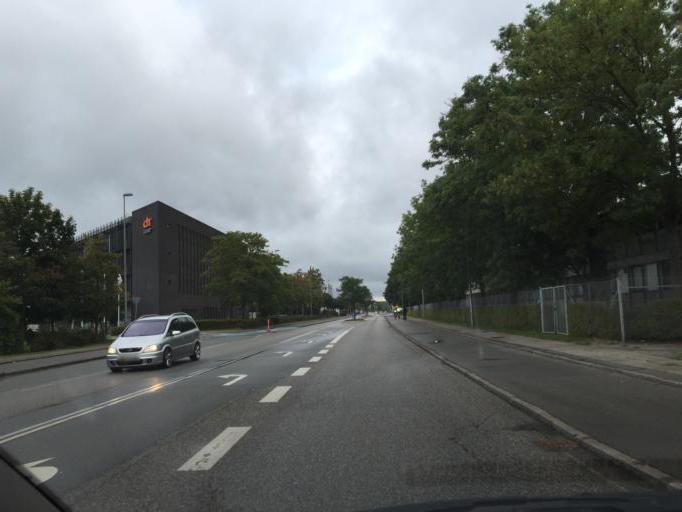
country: DK
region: Capital Region
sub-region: Gladsaxe Municipality
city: Buddinge
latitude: 55.7310
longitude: 12.4768
